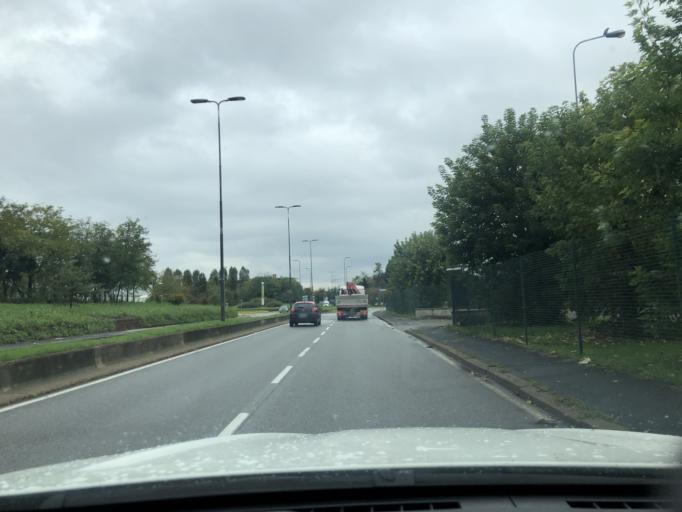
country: IT
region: Lombardy
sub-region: Citta metropolitana di Milano
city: Settimo Milanese
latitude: 45.4600
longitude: 9.0685
